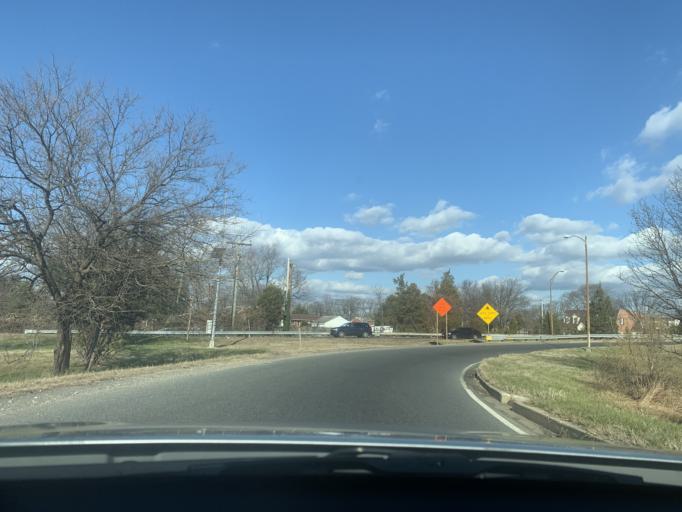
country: US
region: Maryland
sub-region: Prince George's County
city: Forestville
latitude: 38.8403
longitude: -76.8678
